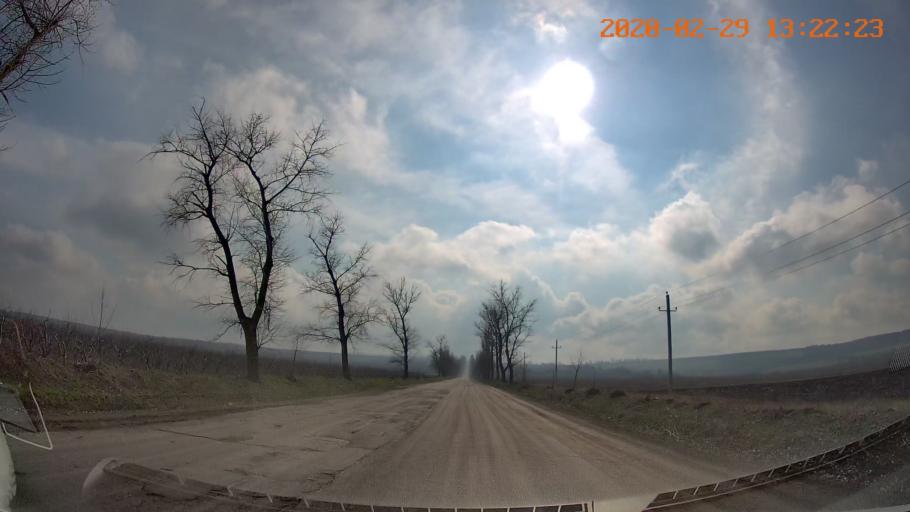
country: MD
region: Telenesti
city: Camenca
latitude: 47.9612
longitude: 28.6280
